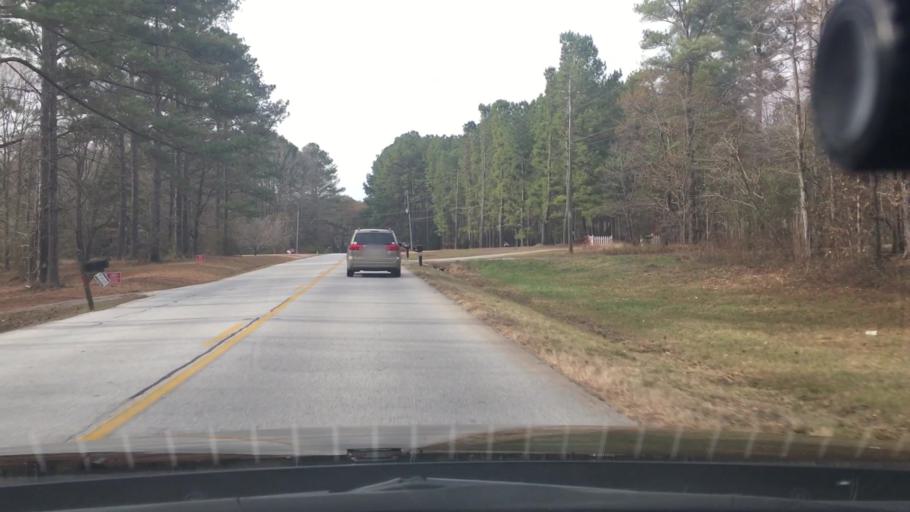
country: US
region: Georgia
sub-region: Coweta County
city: Senoia
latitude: 33.3269
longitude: -84.5012
